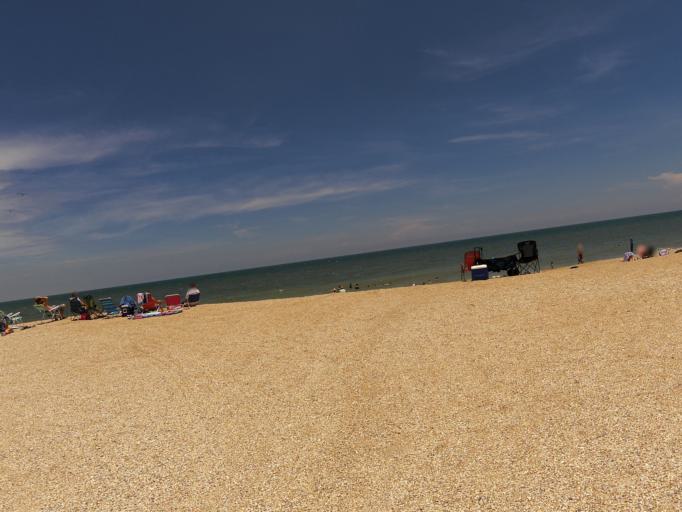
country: US
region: Florida
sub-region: Saint Johns County
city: Palm Valley
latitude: 30.1168
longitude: -81.3449
